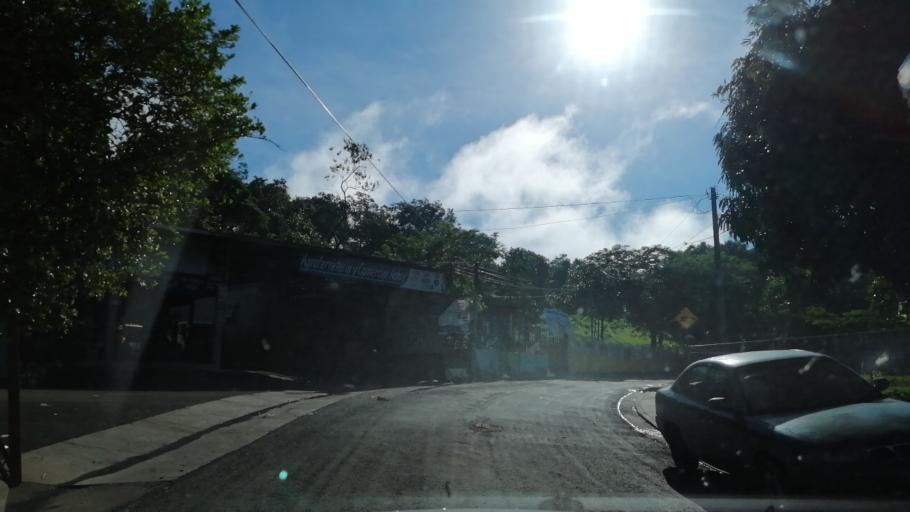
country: SV
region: Morazan
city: Cacaopera
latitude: 13.7753
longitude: -88.0850
